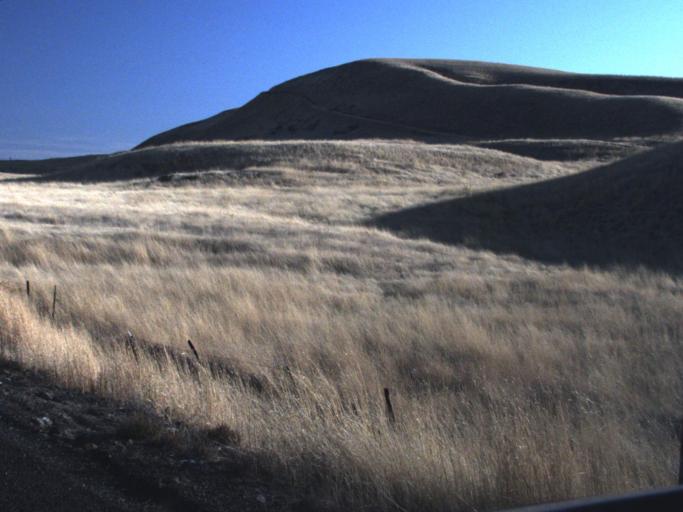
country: US
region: Washington
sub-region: Walla Walla County
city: Waitsburg
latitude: 46.6436
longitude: -118.2466
